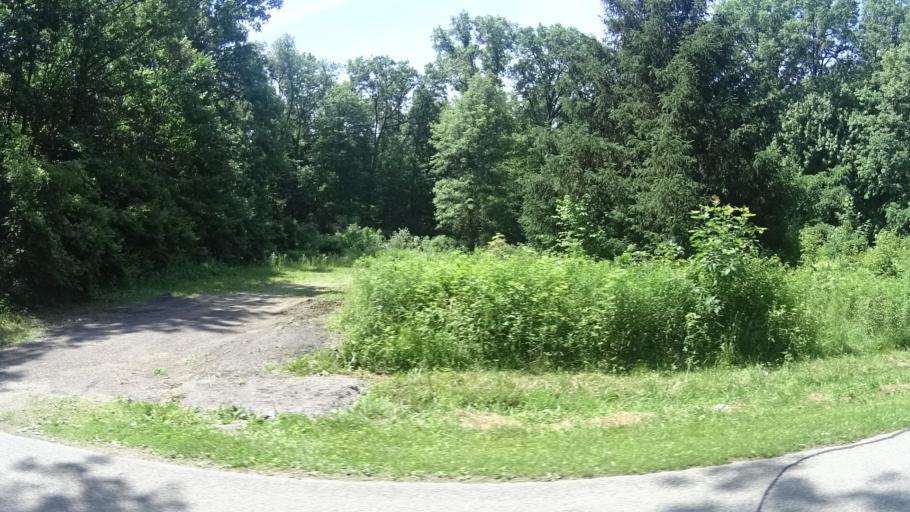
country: US
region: Ohio
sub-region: Erie County
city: Huron
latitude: 41.3525
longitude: -82.4710
